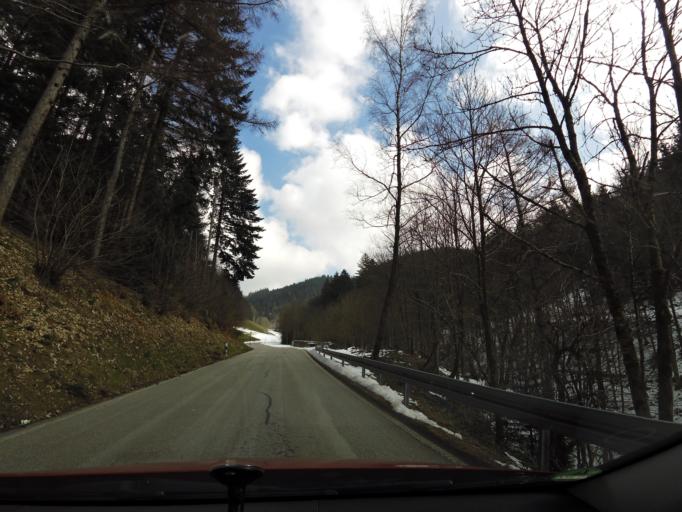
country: DE
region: Baden-Wuerttemberg
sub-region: Freiburg Region
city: Seebach
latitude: 48.5461
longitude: 8.1853
